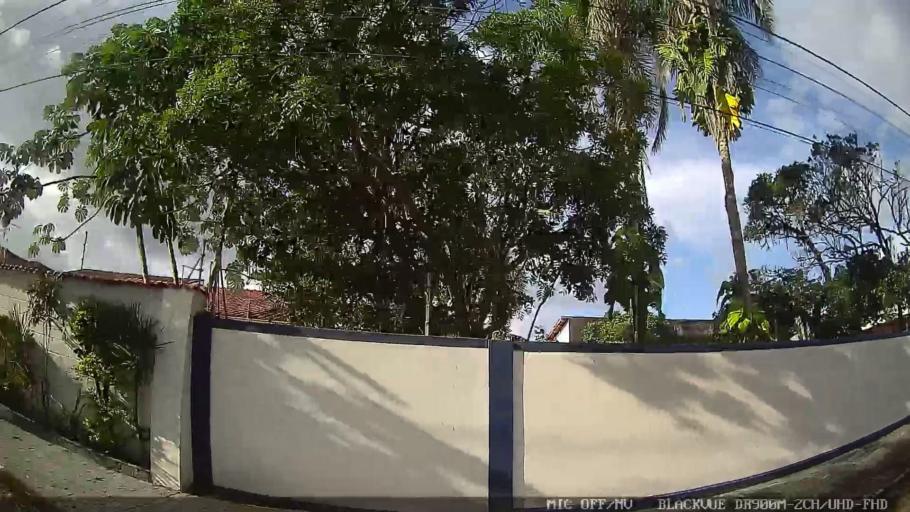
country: BR
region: Sao Paulo
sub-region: Itanhaem
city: Itanhaem
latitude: -24.1973
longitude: -46.8083
